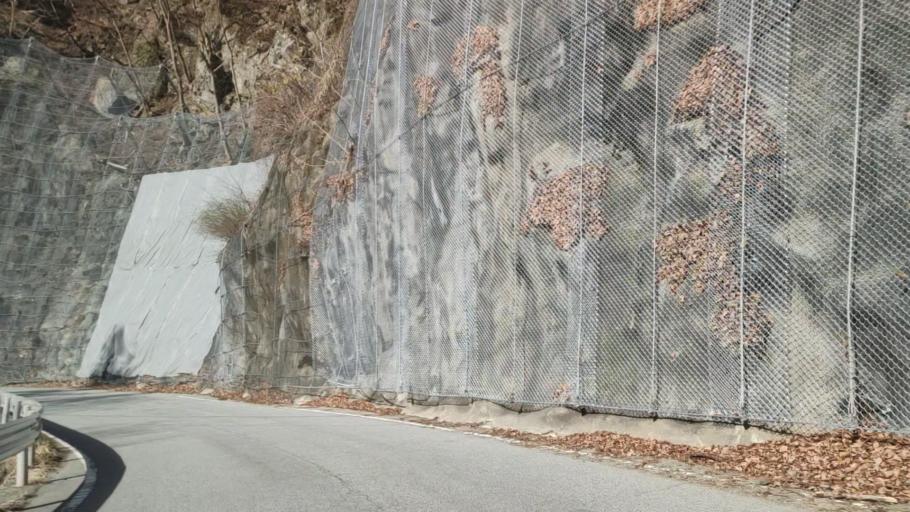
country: JP
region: Yamanashi
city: Fujikawaguchiko
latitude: 35.5345
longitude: 138.6226
